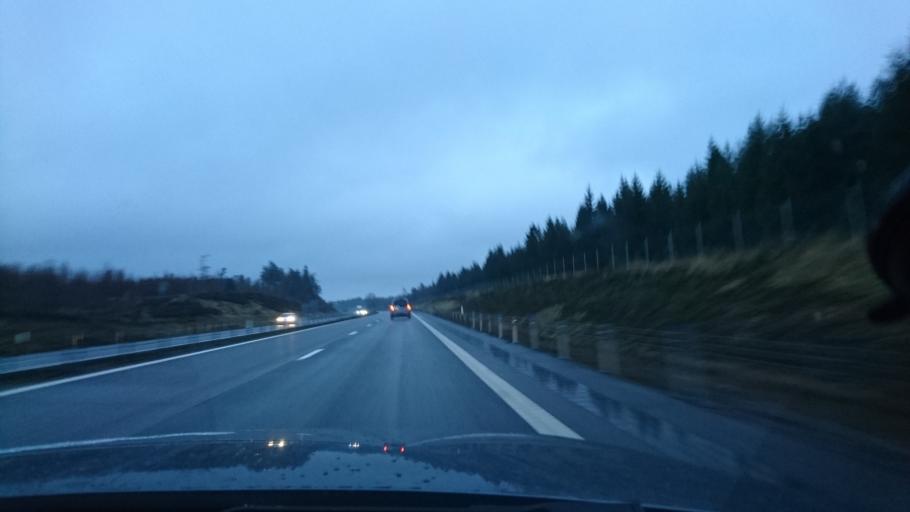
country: SE
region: Kronoberg
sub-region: Markaryds Kommun
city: Markaryd
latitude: 56.3644
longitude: 13.4864
